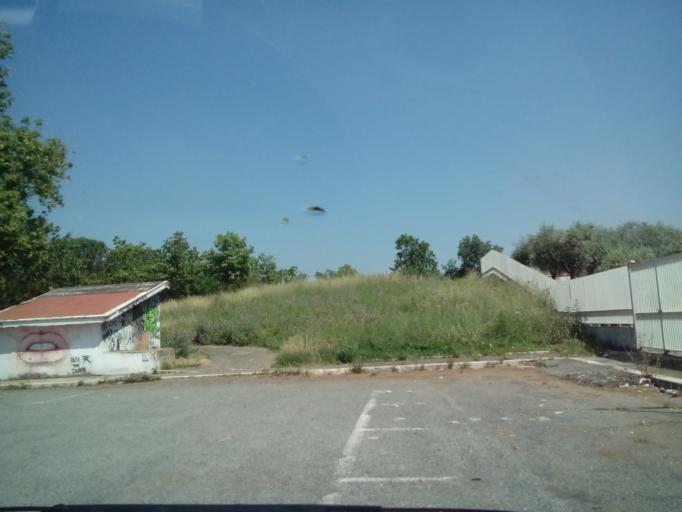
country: IT
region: Latium
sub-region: Citta metropolitana di Roma Capitale
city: Rome
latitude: 41.8825
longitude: 12.5846
